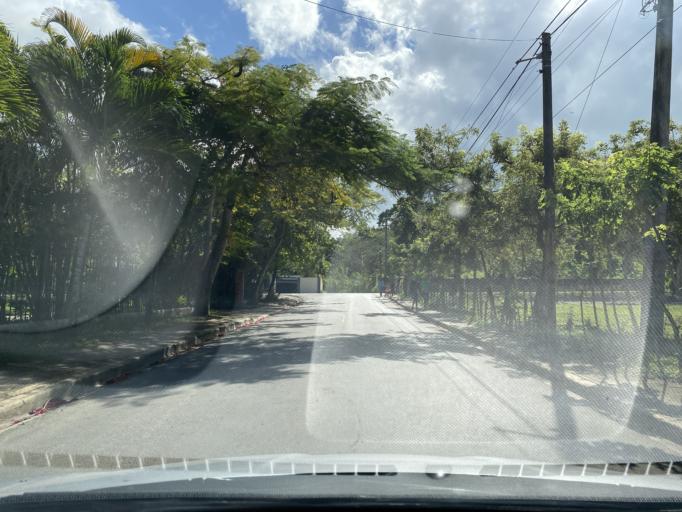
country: DO
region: Samana
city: Las Terrenas
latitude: 19.3116
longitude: -69.5285
